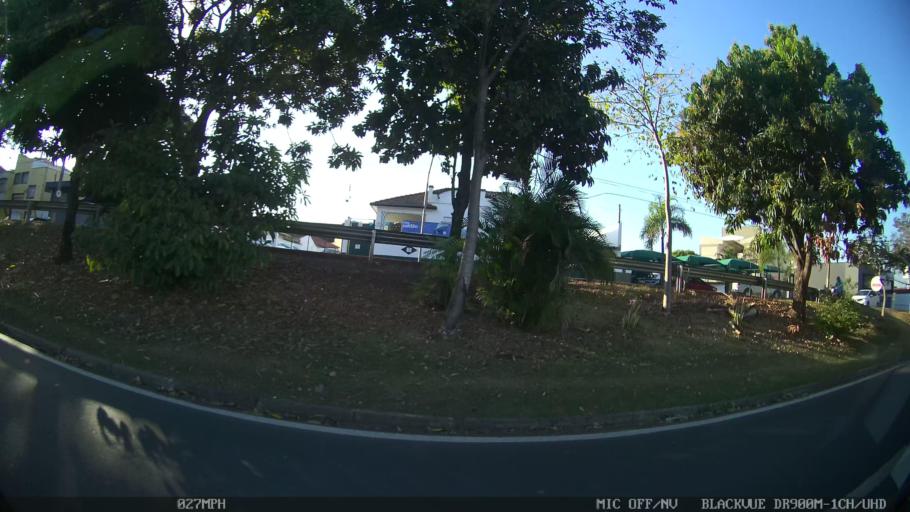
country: BR
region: Sao Paulo
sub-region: Piracicaba
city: Piracicaba
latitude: -22.7036
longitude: -47.6535
